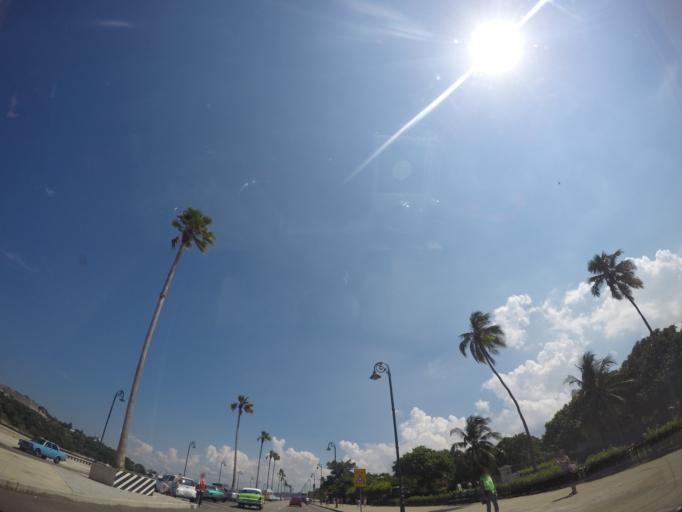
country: CU
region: La Habana
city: Centro Habana
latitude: 23.1438
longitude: -82.3529
